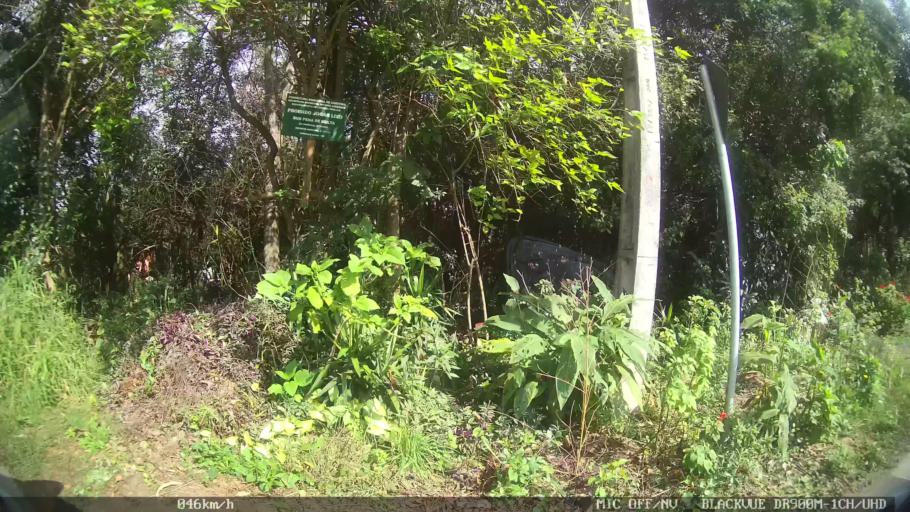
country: BR
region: Parana
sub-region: Curitiba
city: Curitiba
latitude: -25.3763
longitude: -49.2550
